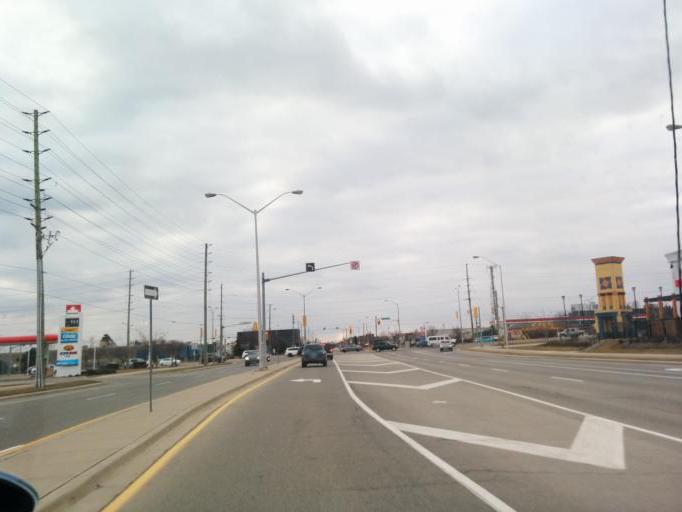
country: CA
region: Ontario
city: Burlington
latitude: 43.3928
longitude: -79.7514
